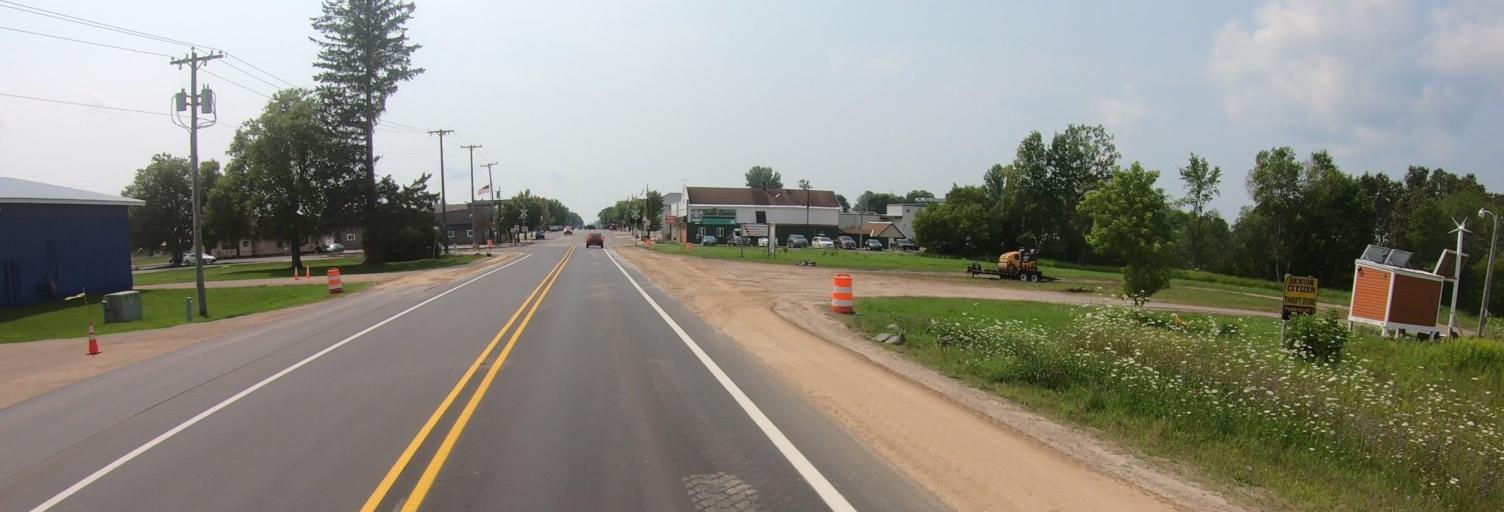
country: US
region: Michigan
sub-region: Luce County
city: Newberry
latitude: 46.3575
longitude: -85.5099
